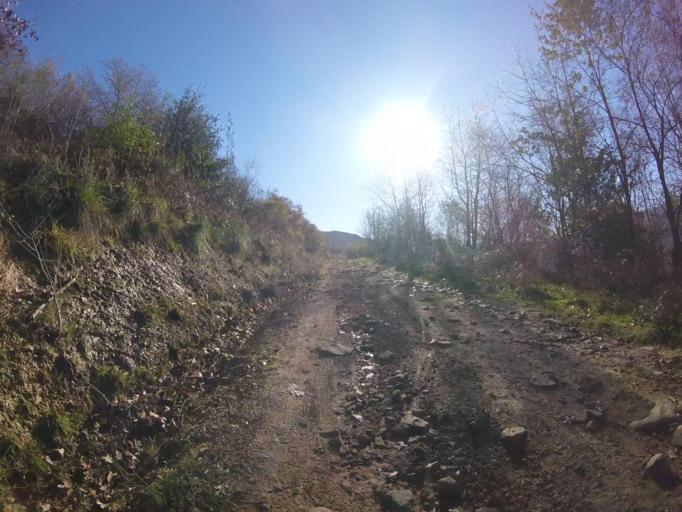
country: FR
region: Aquitaine
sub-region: Departement des Pyrenees-Atlantiques
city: Urrugne
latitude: 43.3191
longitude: -1.7284
